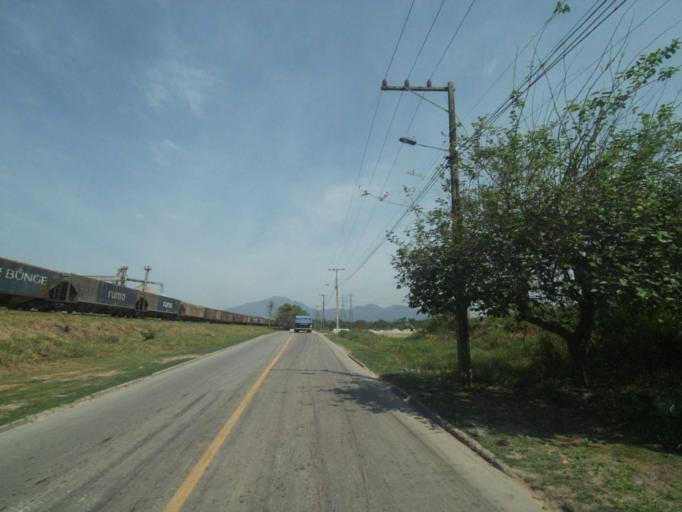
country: BR
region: Parana
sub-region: Paranagua
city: Paranagua
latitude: -25.5482
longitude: -48.5532
